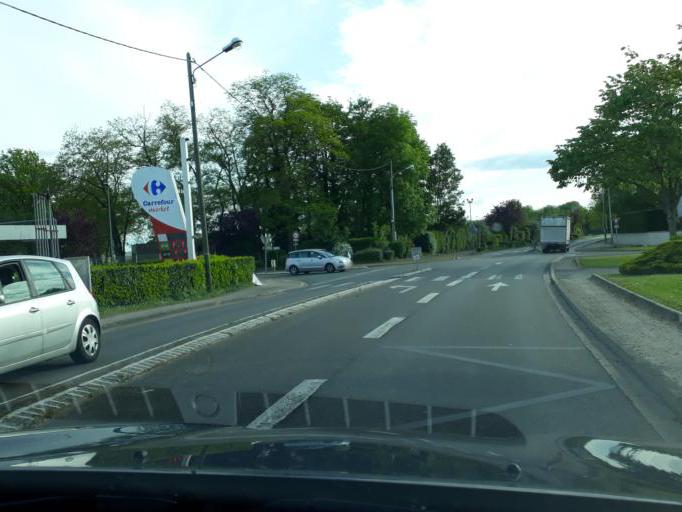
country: FR
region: Centre
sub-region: Departement du Loiret
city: Ingre
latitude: 47.9243
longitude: 1.8450
